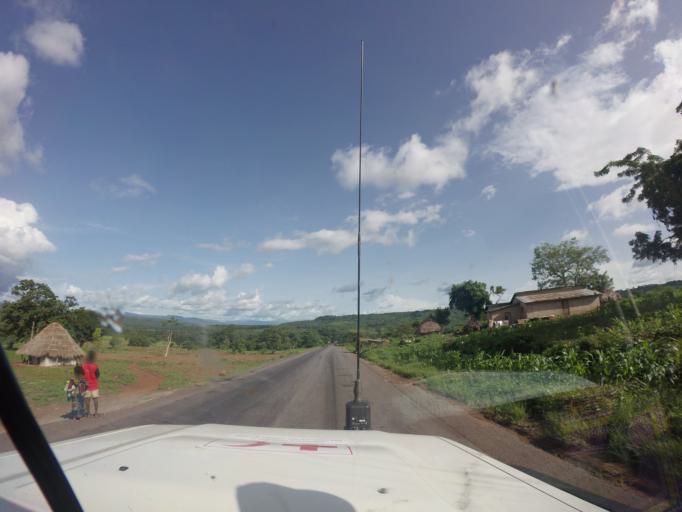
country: GN
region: Mamou
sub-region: Mamou Prefecture
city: Mamou
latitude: 10.1904
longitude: -12.4581
